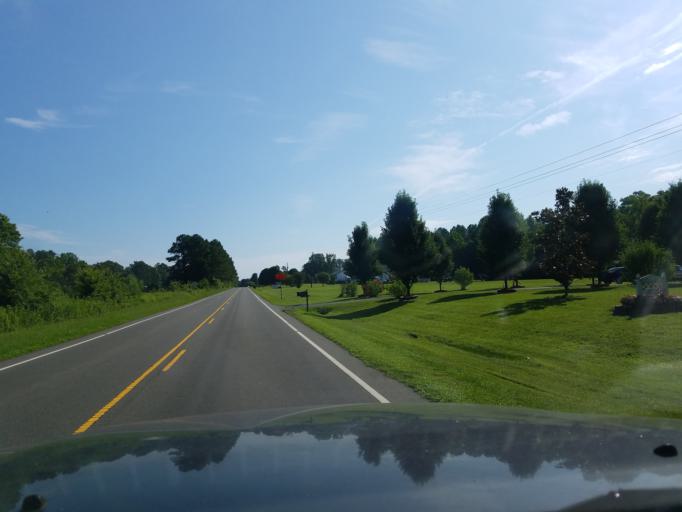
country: US
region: North Carolina
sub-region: Granville County
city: Oxford
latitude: 36.2655
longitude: -78.6511
